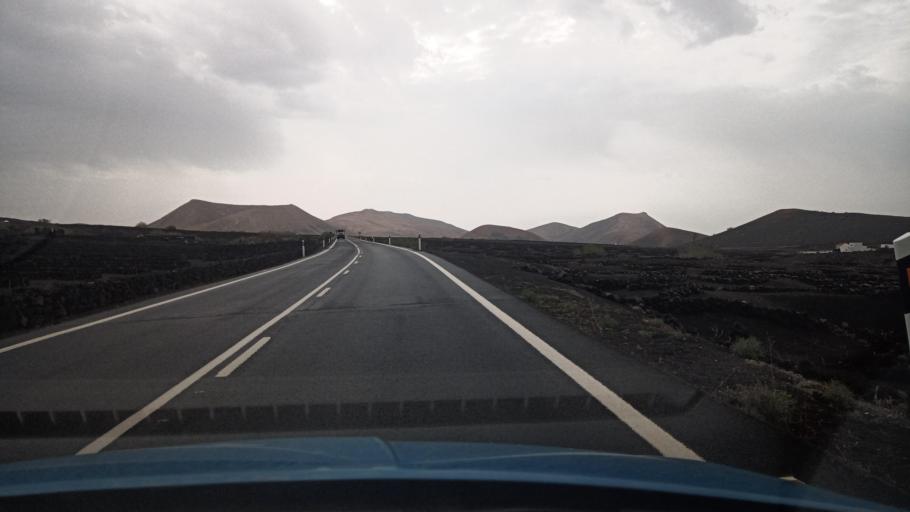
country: ES
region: Canary Islands
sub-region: Provincia de Las Palmas
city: Yaiza
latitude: 28.9602
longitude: -13.7294
